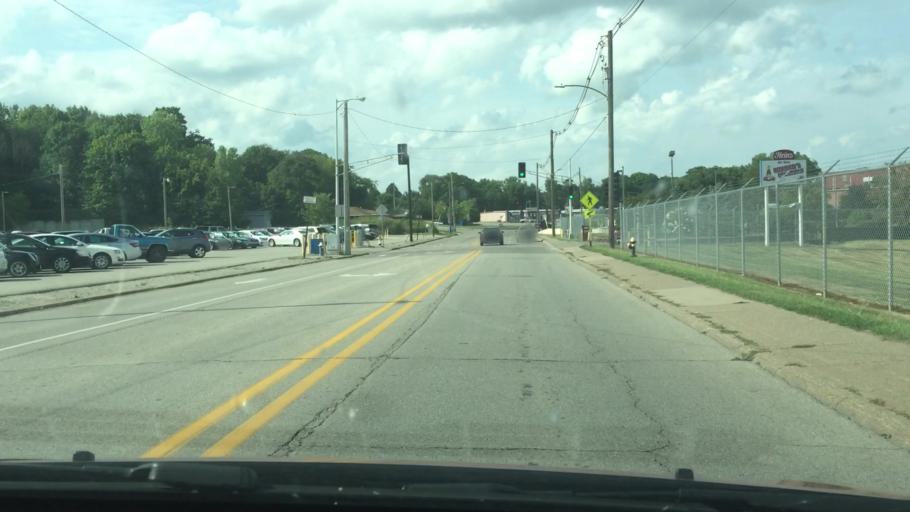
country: US
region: Iowa
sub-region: Muscatine County
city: Muscatine
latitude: 41.4365
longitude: -91.0431
